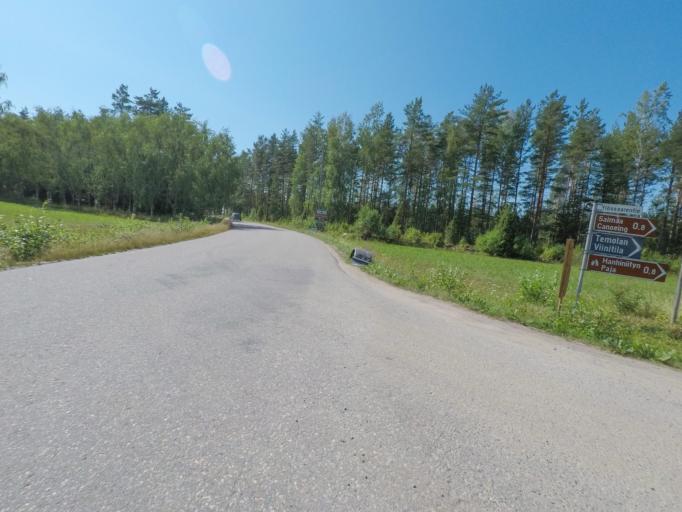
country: FI
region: Southern Savonia
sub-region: Mikkeli
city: Puumala
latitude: 61.4511
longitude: 28.1592
